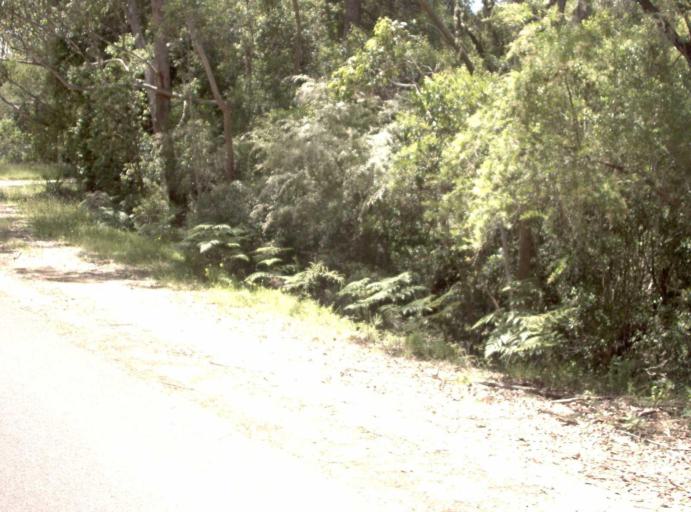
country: AU
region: New South Wales
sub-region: Bombala
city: Bombala
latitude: -37.5152
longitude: 148.9285
